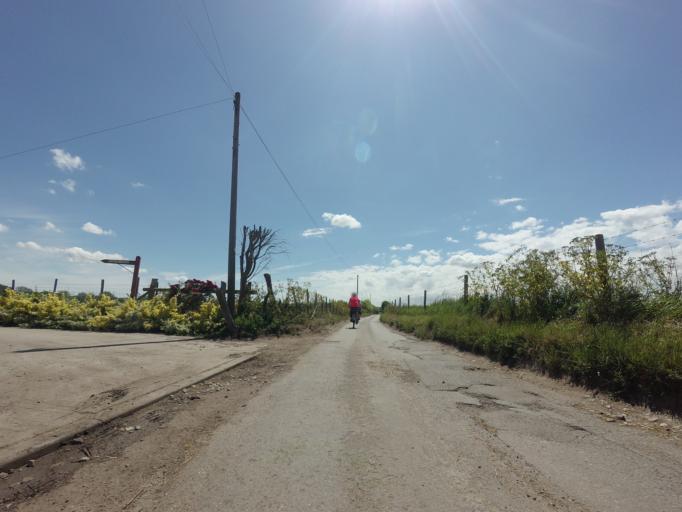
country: GB
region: England
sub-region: Medway
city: Cooling
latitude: 51.4590
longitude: 0.5137
